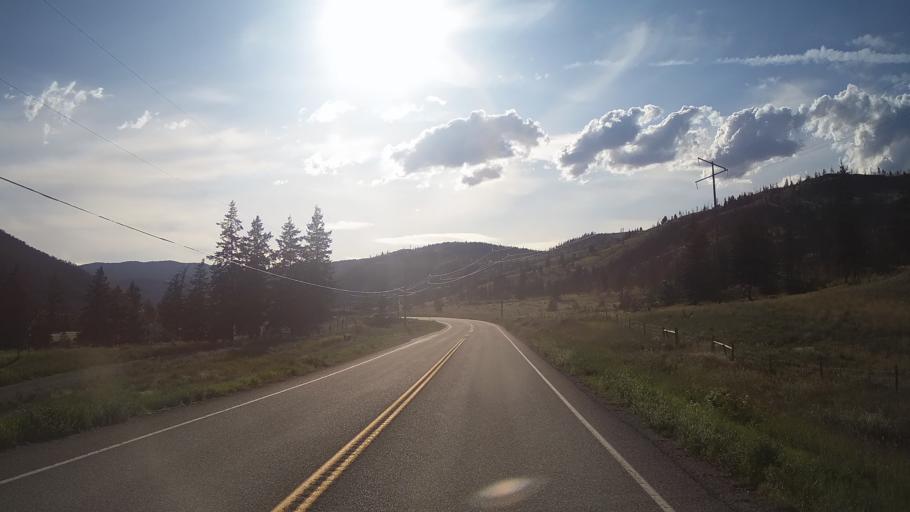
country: CA
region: British Columbia
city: Cache Creek
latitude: 50.8869
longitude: -121.4605
